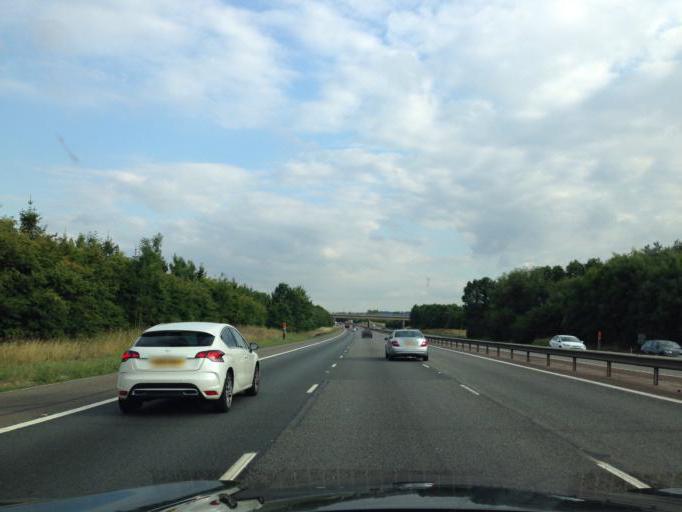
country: GB
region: England
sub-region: Warwickshire
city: Harbury
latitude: 52.1754
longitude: -1.4443
